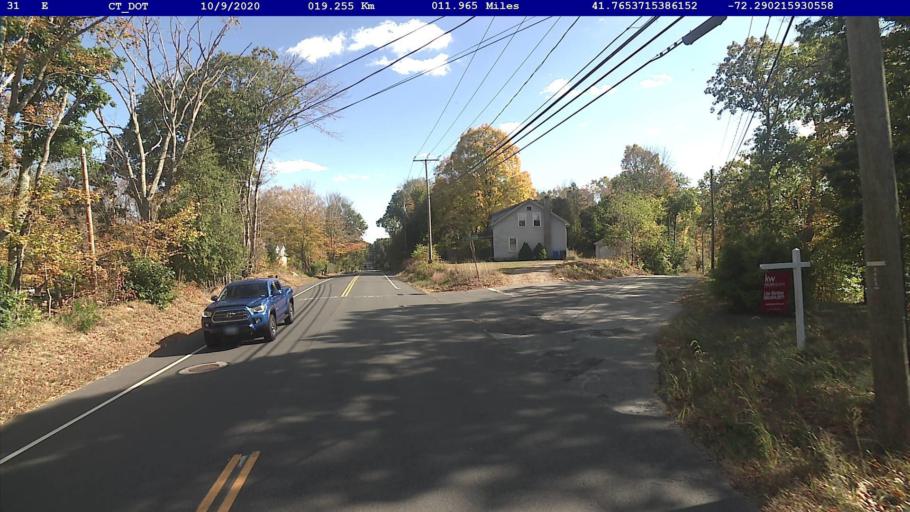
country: US
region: Connecticut
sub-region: Tolland County
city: South Coventry
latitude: 41.7654
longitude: -72.2902
